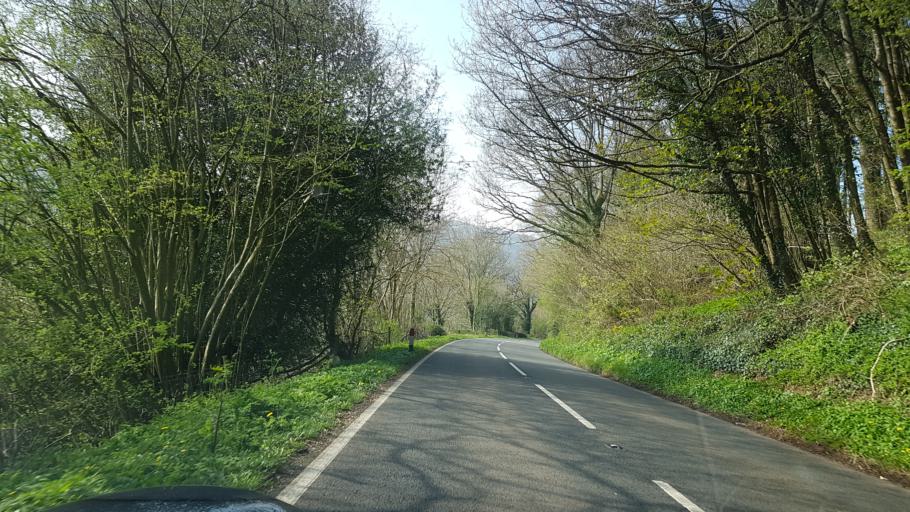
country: GB
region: Wales
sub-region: Monmouthshire
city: Tintern
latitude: 51.7593
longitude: -2.6676
